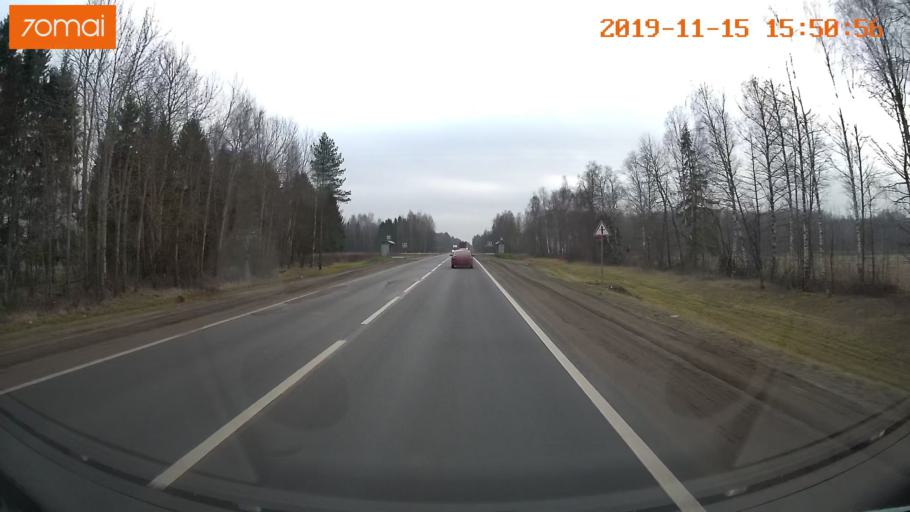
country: RU
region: Jaroslavl
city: Yaroslavl
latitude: 57.9004
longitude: 40.0112
